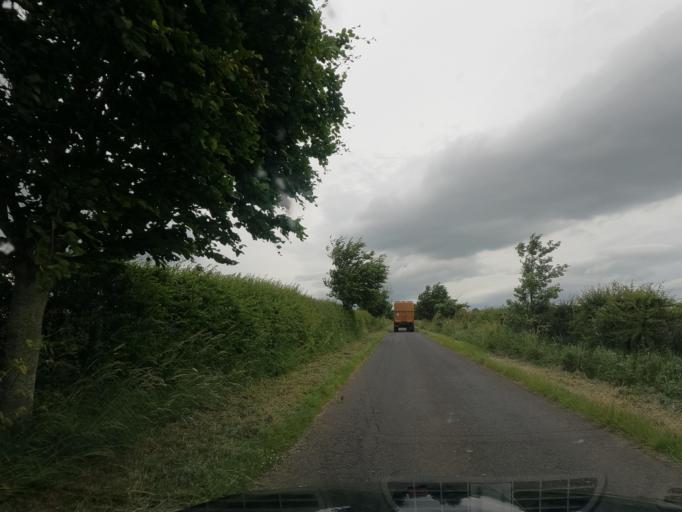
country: GB
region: England
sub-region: Northumberland
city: Lowick
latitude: 55.5729
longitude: -1.9174
